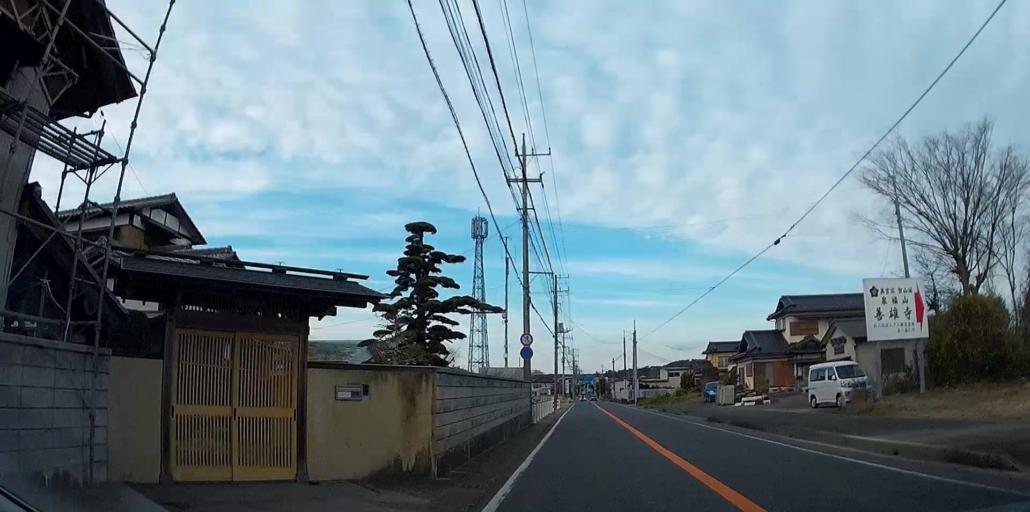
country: JP
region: Chiba
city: Kisarazu
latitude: 35.3631
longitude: 140.0581
